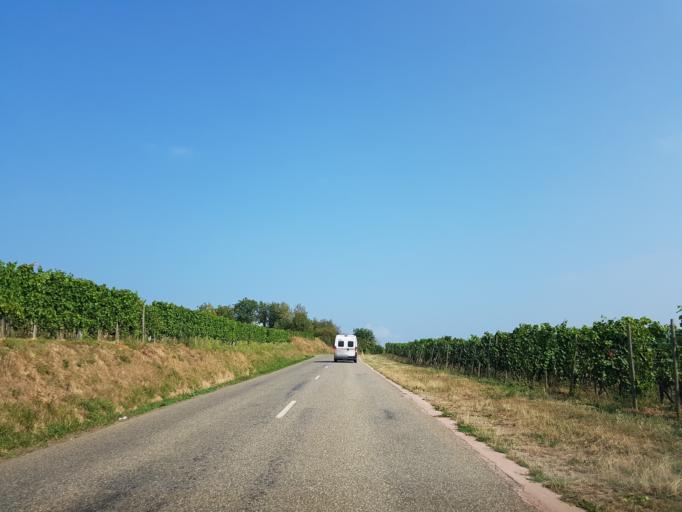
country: FR
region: Alsace
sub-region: Departement du Haut-Rhin
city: Eguisheim
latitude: 48.0371
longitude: 7.3114
